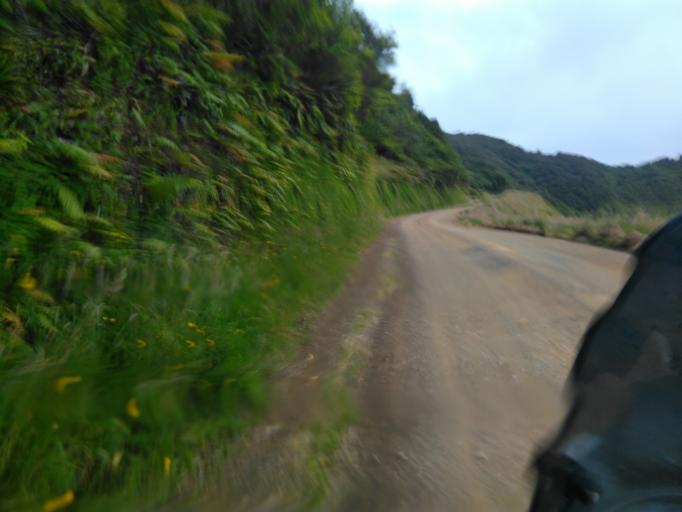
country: NZ
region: Bay of Plenty
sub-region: Opotiki District
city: Opotiki
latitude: -38.0962
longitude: 177.4856
